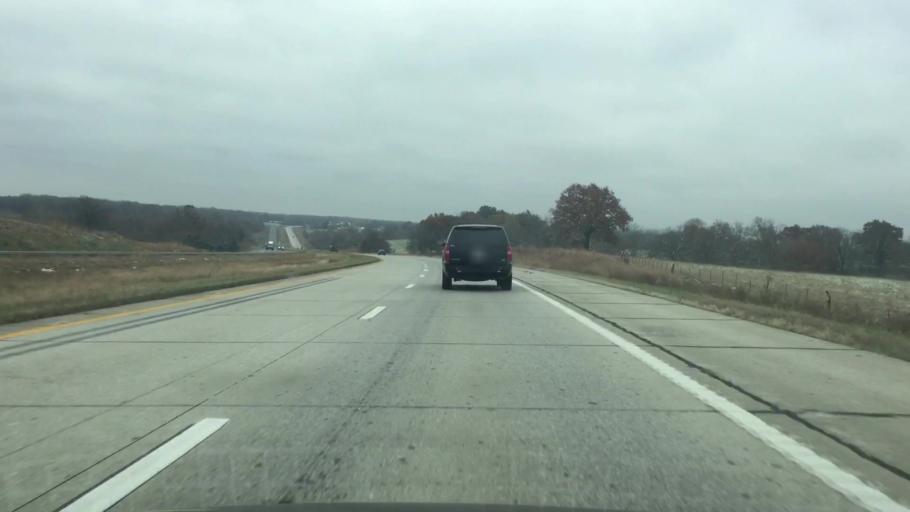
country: US
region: Missouri
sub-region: Saint Clair County
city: Osceola
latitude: 38.0248
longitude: -93.6730
